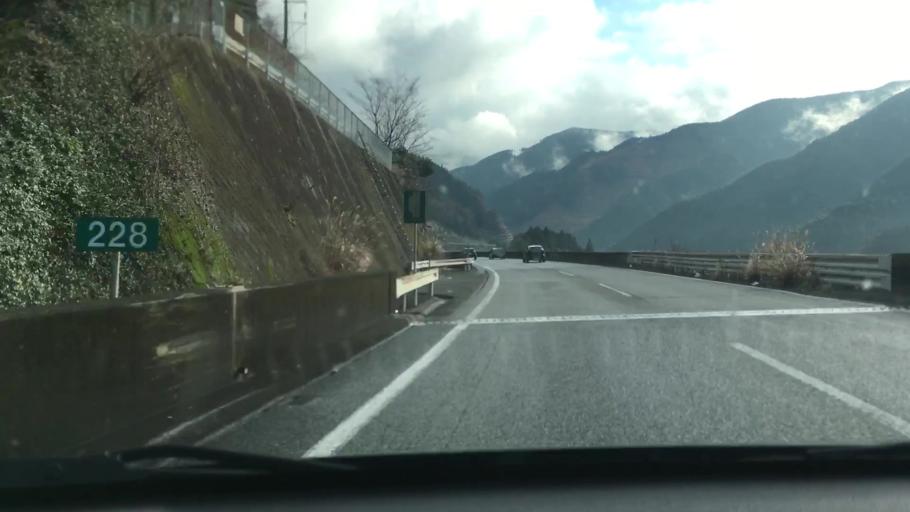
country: JP
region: Kumamoto
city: Yatsushiro
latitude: 32.4119
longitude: 130.6956
